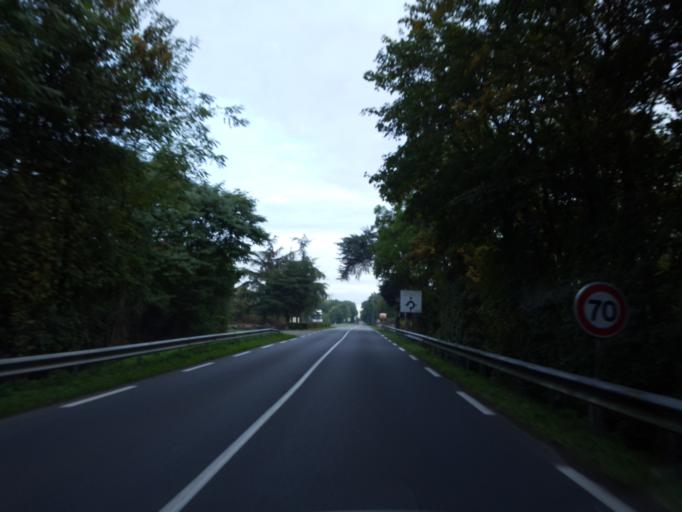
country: FR
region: Pays de la Loire
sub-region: Departement de la Loire-Atlantique
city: Haute-Goulaine
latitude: 47.2139
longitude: -1.4383
